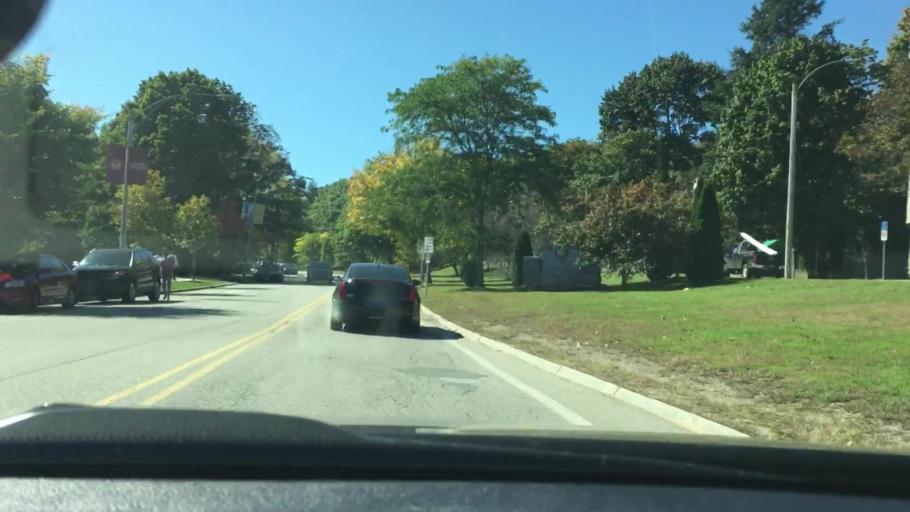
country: US
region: Massachusetts
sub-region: Middlesex County
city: Watertown
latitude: 42.3396
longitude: -71.1683
